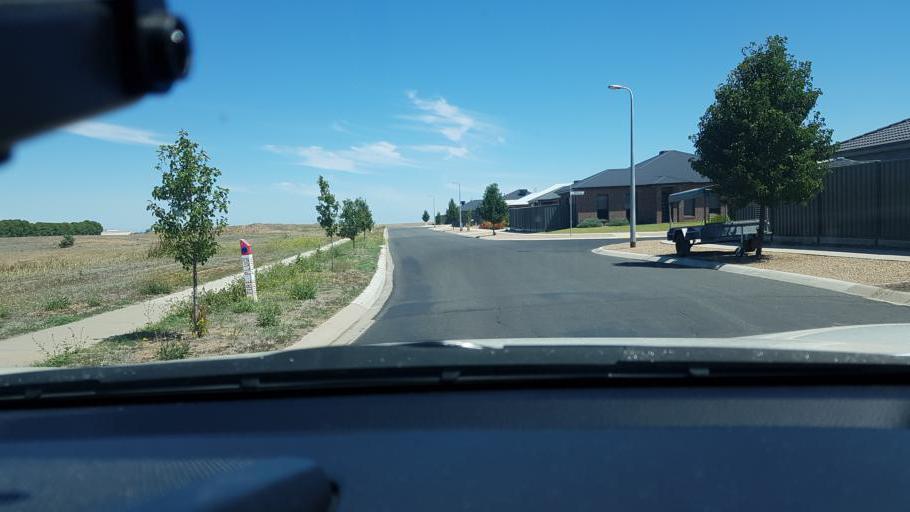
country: AU
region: Victoria
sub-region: Horsham
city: Horsham
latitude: -36.7157
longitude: 142.1783
